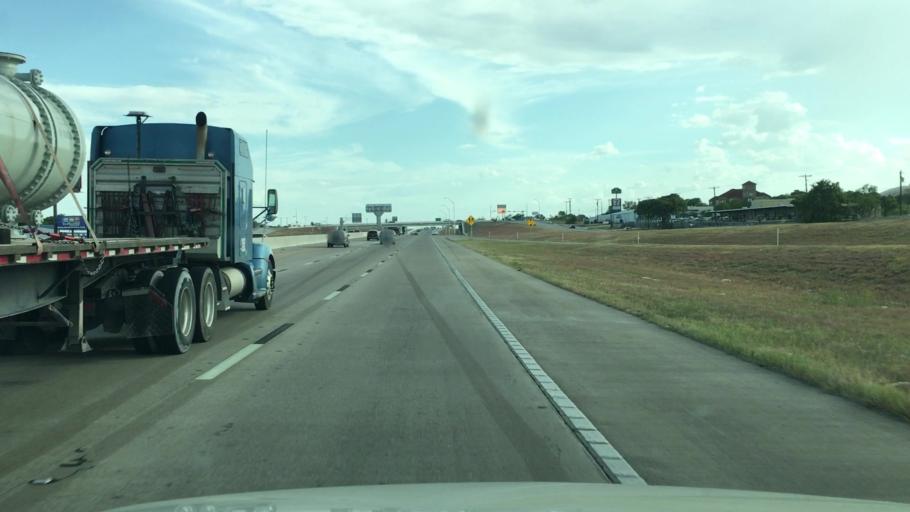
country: US
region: Texas
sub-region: Bell County
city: Belton
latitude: 31.0353
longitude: -97.4723
